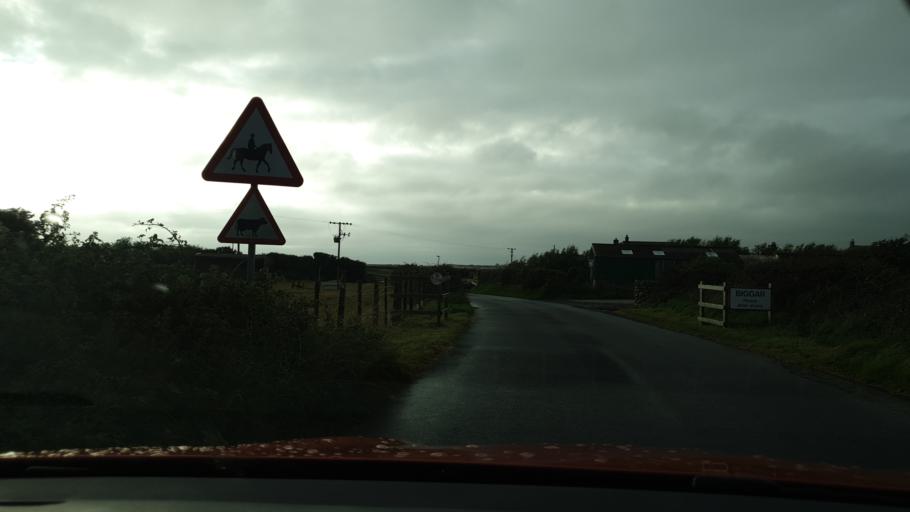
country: GB
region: England
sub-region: Cumbria
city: Barrow in Furness
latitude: 54.0835
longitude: -3.2362
